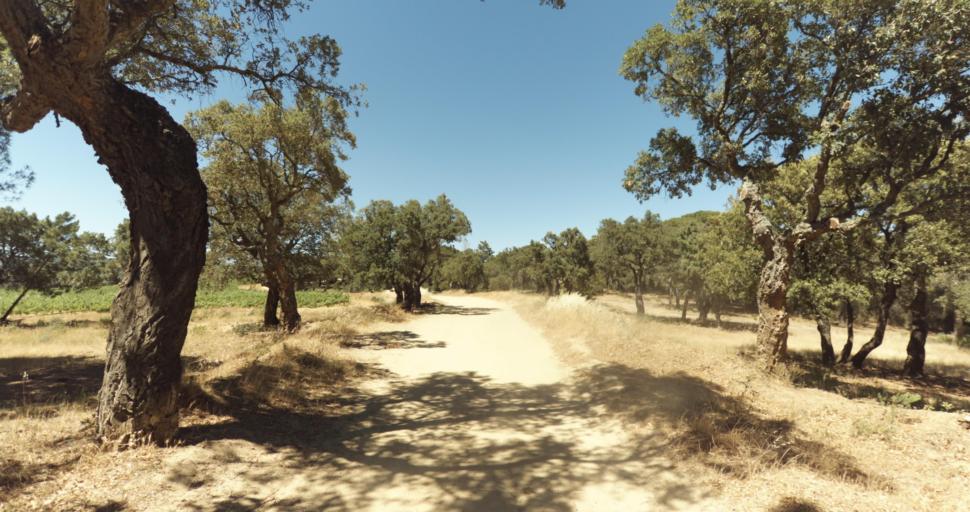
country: FR
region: Provence-Alpes-Cote d'Azur
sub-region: Departement du Var
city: Gassin
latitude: 43.2432
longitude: 6.5610
